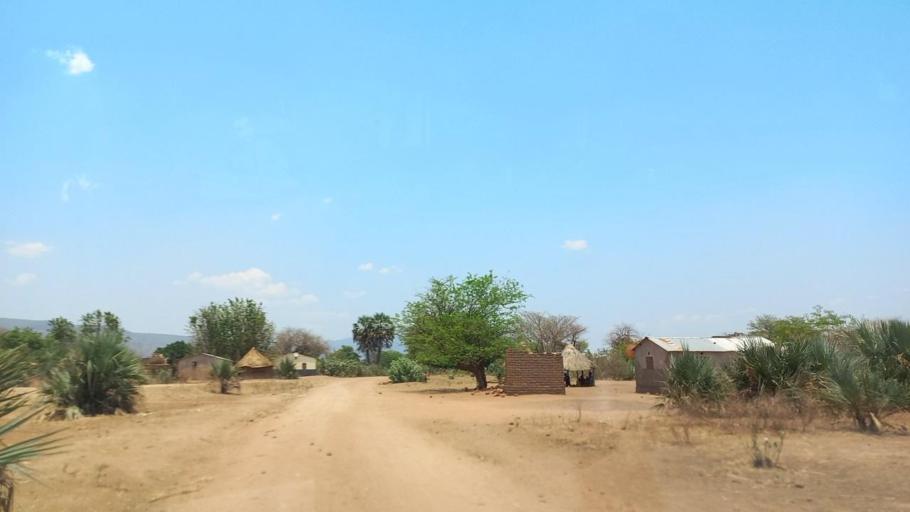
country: ZM
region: Lusaka
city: Luangwa
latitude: -15.1922
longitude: 30.1875
